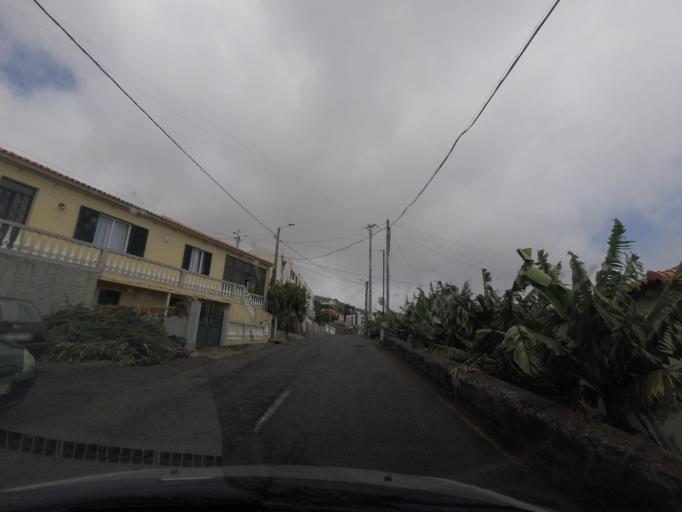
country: PT
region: Madeira
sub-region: Machico
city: Machico
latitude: 32.7022
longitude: -16.7768
